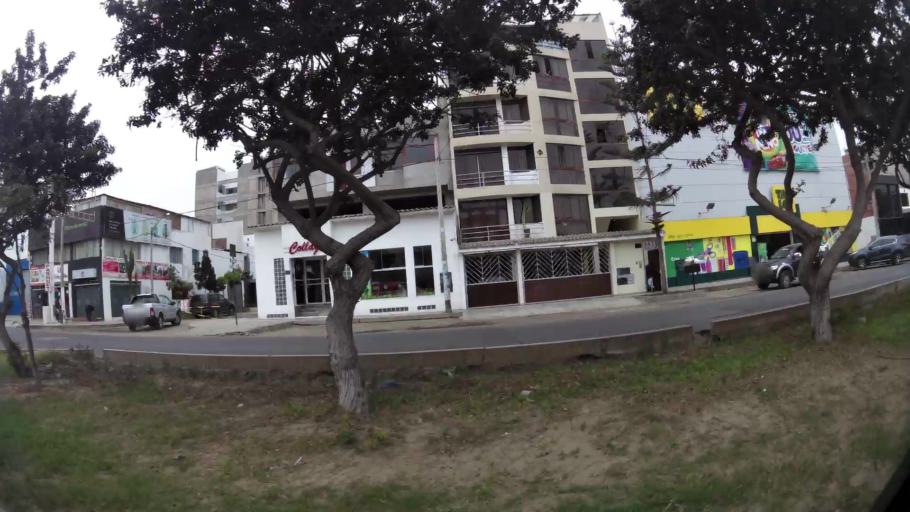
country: PE
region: La Libertad
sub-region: Provincia de Trujillo
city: Buenos Aires
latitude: -8.1335
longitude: -79.0353
